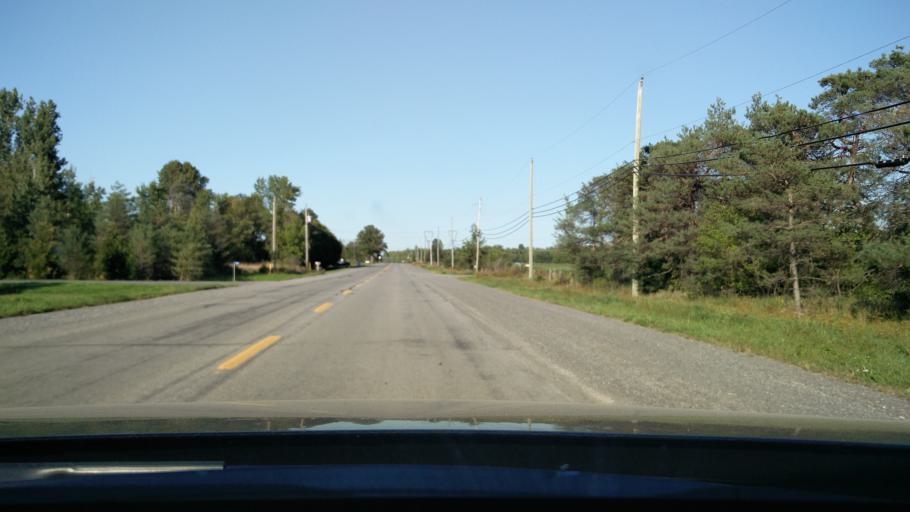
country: CA
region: Ontario
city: Bells Corners
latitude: 45.1605
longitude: -75.8915
